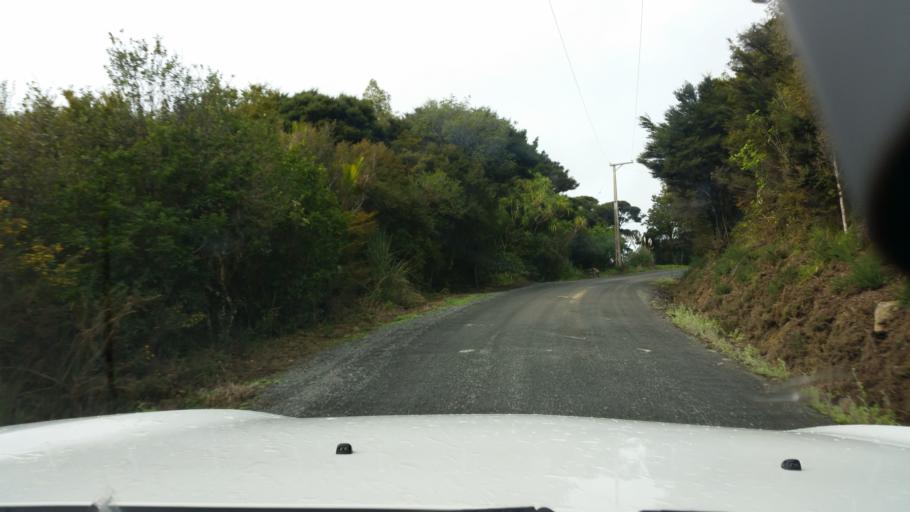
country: NZ
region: Northland
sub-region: Whangarei
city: Ngunguru
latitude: -35.7708
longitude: 174.5347
